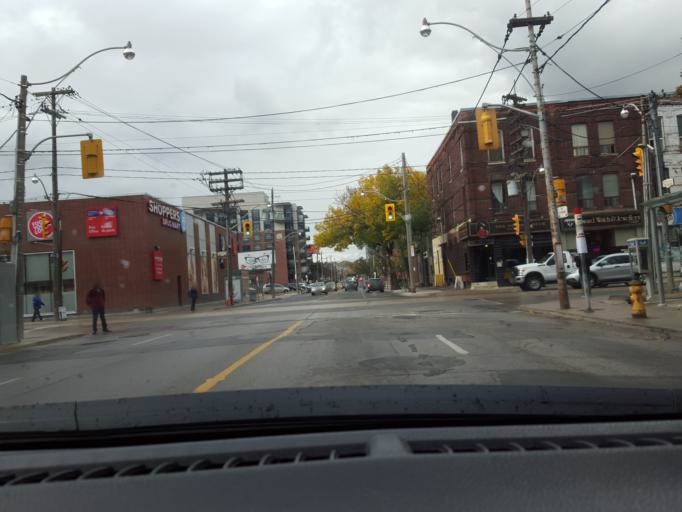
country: CA
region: Ontario
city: Toronto
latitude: 43.6607
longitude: -79.3399
